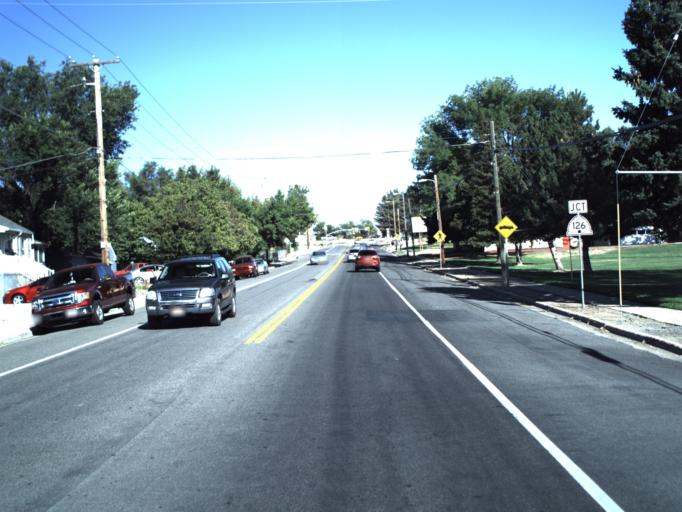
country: US
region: Utah
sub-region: Davis County
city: Sunset
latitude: 41.1398
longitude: -112.0294
